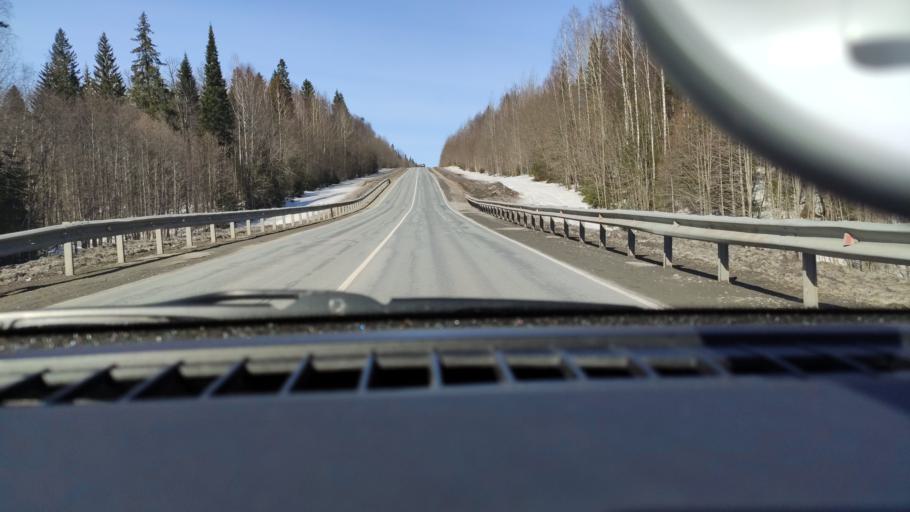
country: RU
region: Perm
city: Perm
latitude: 58.1654
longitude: 56.2406
